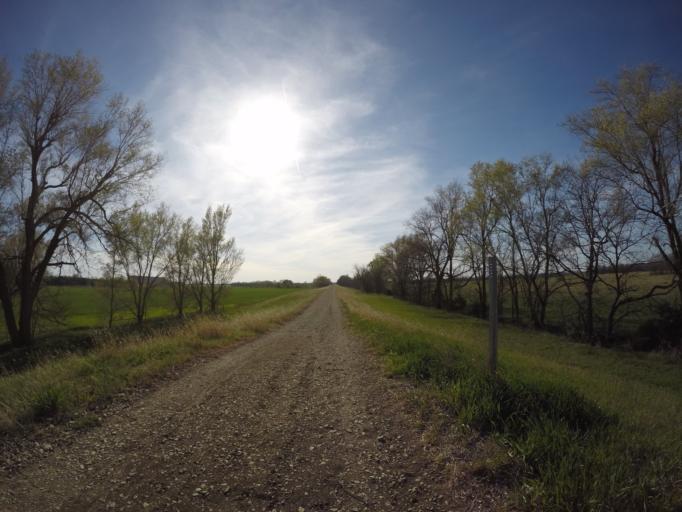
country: US
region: Kansas
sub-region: Saline County
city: Salina
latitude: 38.8633
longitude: -97.5806
